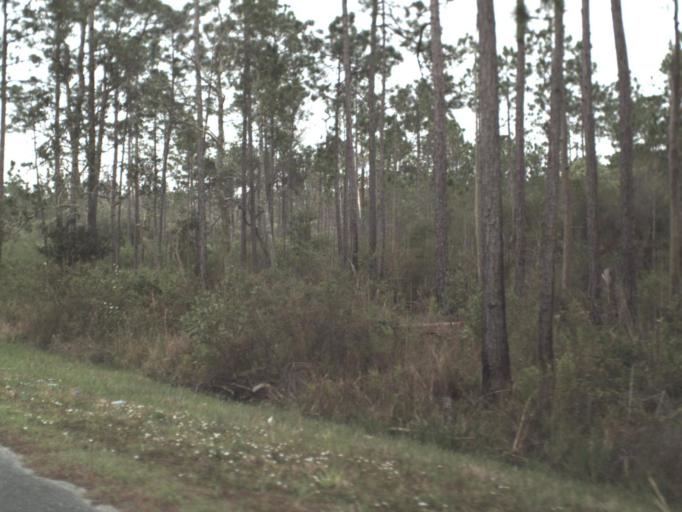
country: US
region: Florida
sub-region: Franklin County
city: Eastpoint
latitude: 29.8089
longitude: -84.8399
